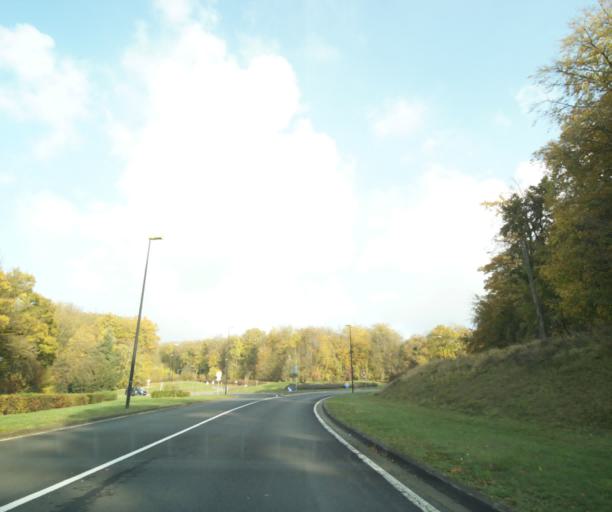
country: FR
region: Lorraine
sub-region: Departement de Meurthe-et-Moselle
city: Briey
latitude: 49.2587
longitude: 5.9346
